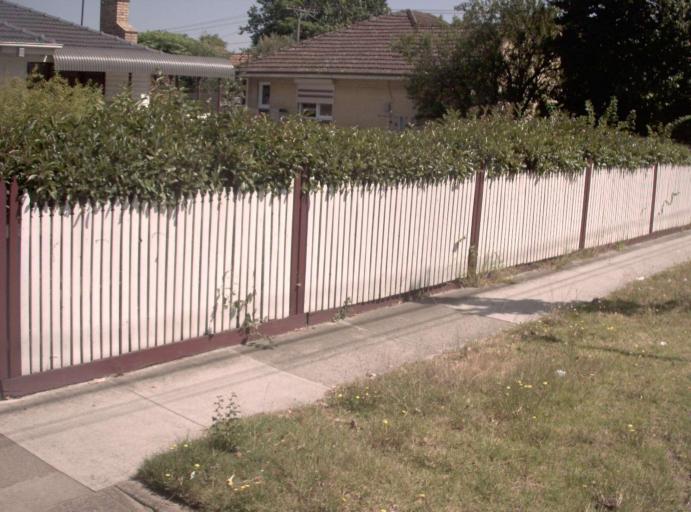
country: AU
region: Victoria
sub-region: Monash
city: Oakleigh South
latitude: -37.9276
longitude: 145.0817
